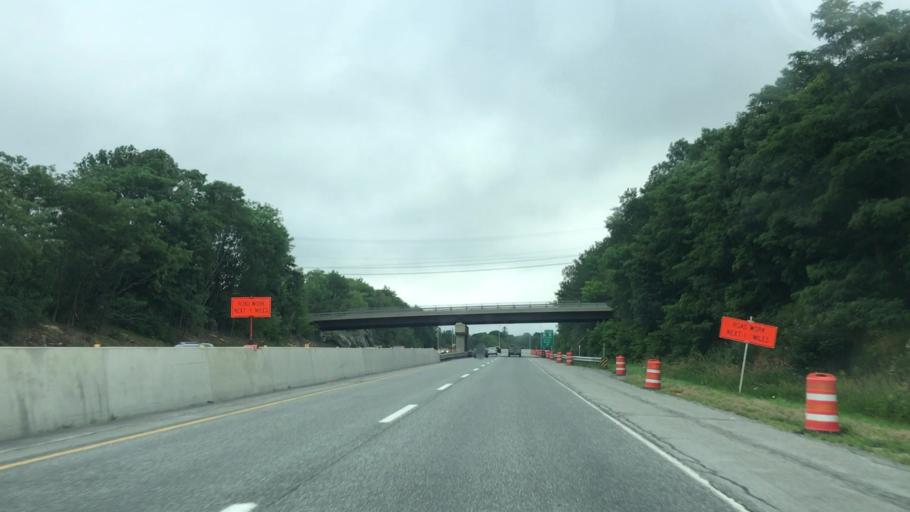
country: US
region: Maine
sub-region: Penobscot County
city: Bangor
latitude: 44.8209
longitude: -68.7677
